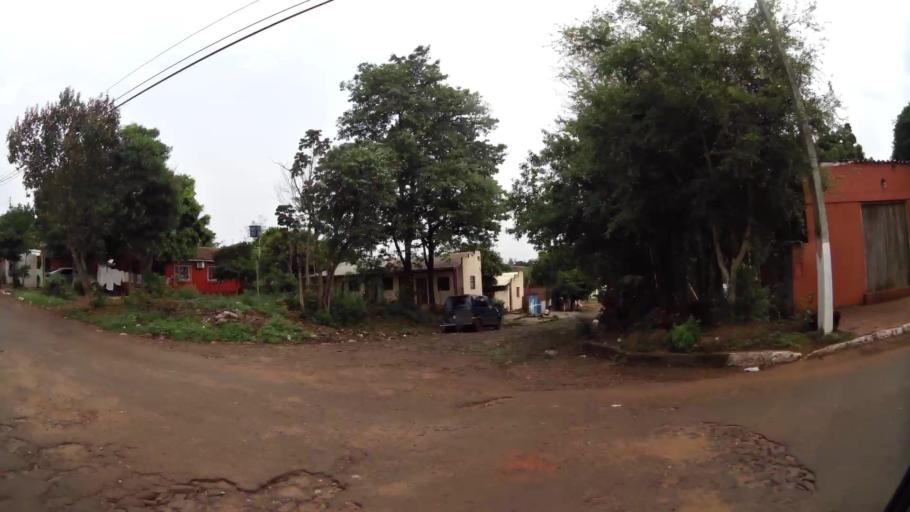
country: BR
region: Parana
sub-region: Foz Do Iguacu
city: Foz do Iguacu
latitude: -25.5637
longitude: -54.6051
